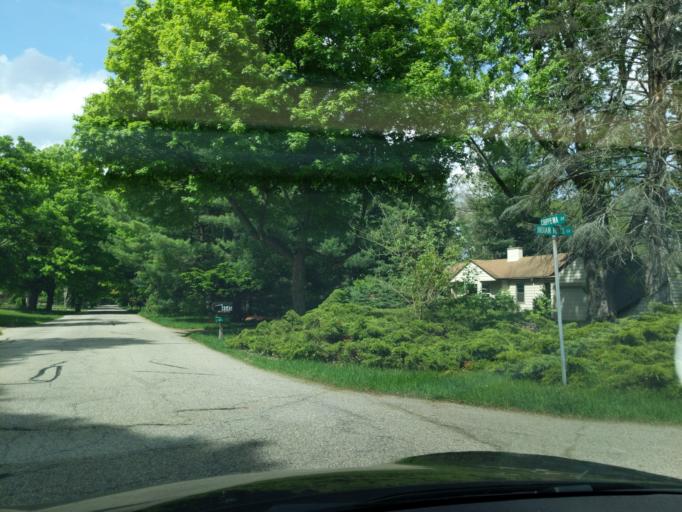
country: US
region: Michigan
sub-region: Ingham County
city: Okemos
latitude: 42.7131
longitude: -84.4397
